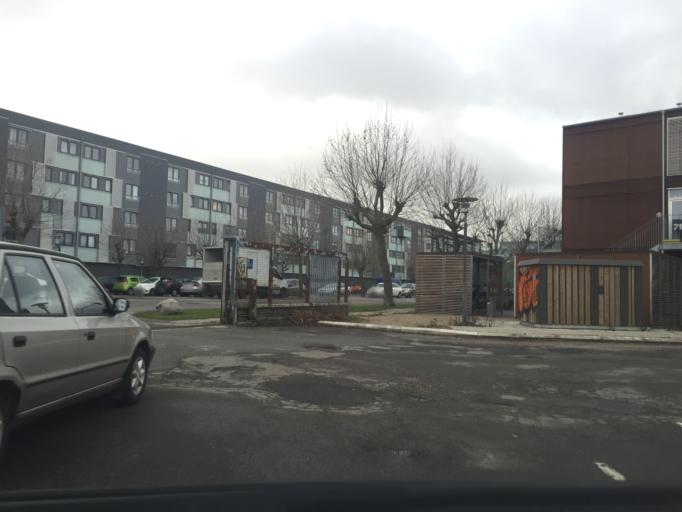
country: DK
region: Capital Region
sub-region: Kobenhavn
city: Christianshavn
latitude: 55.6591
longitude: 12.5958
